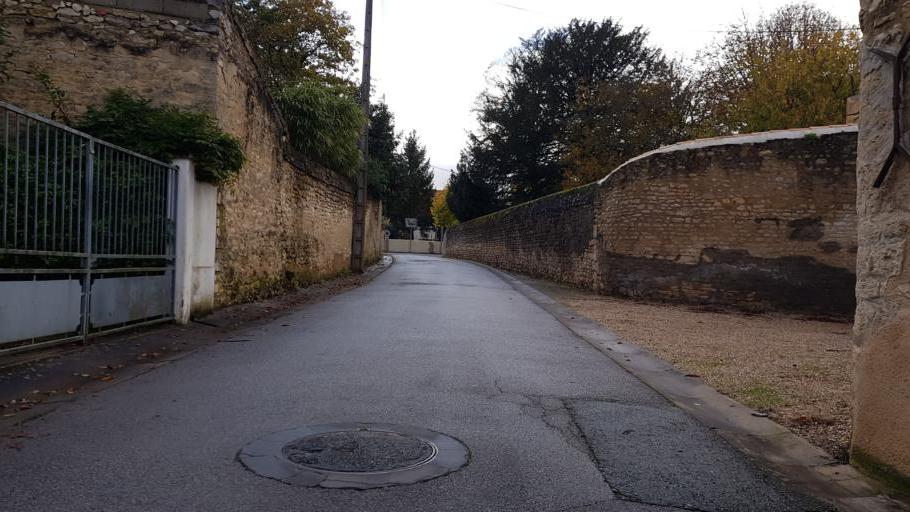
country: FR
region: Poitou-Charentes
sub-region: Departement de la Vienne
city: Chasseneuil-du-Poitou
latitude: 46.6488
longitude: 0.3722
